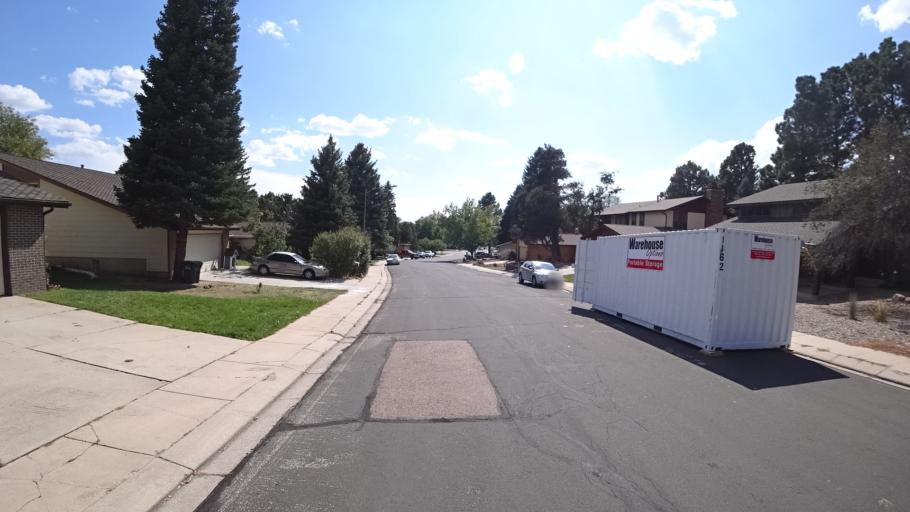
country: US
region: Colorado
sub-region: El Paso County
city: Cimarron Hills
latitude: 38.8769
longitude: -104.7520
